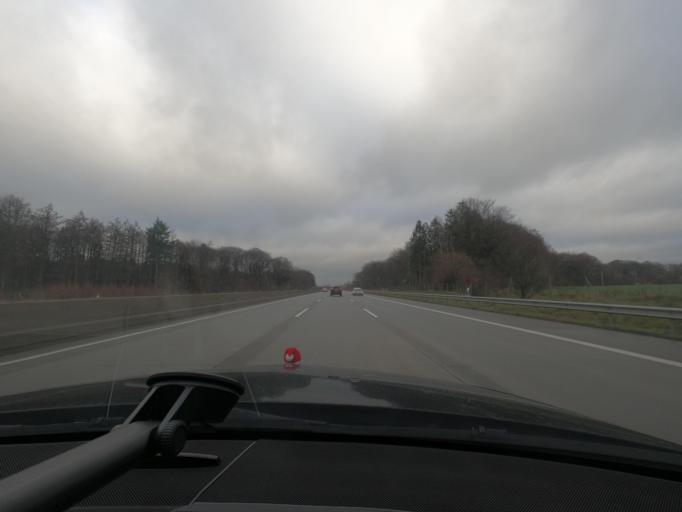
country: DE
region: Schleswig-Holstein
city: Bimohlen
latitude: 53.9311
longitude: 9.9432
